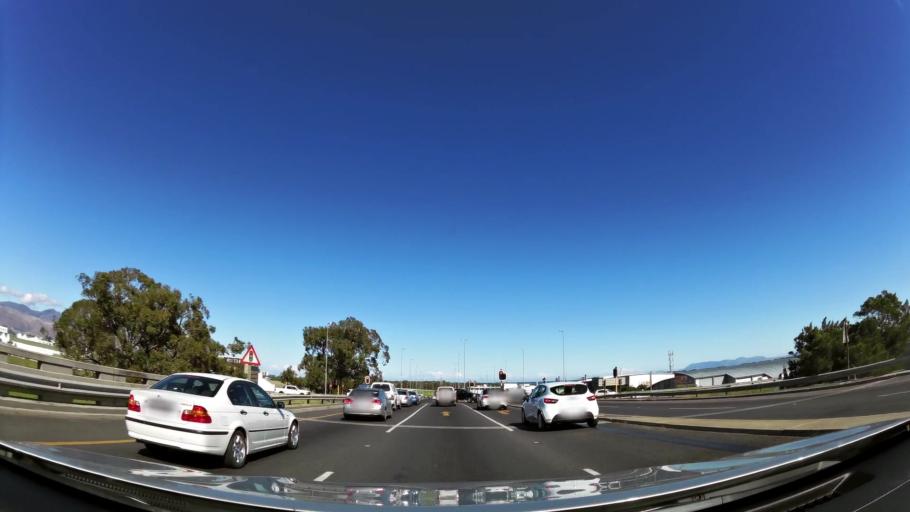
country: ZA
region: Western Cape
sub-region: Cape Winelands District Municipality
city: Stellenbosch
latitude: -34.0773
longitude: 18.8207
